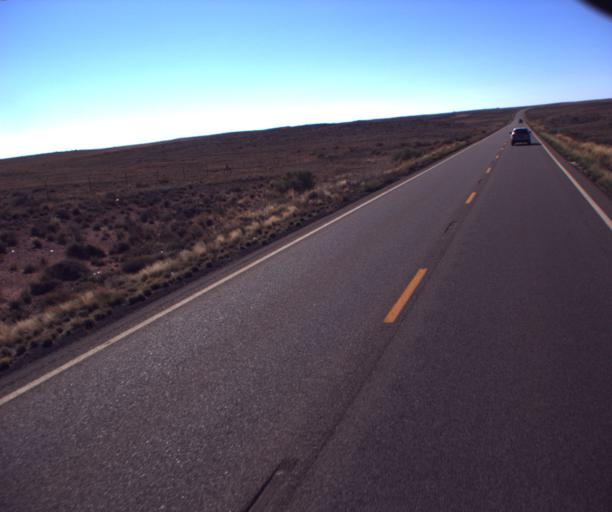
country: US
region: Arizona
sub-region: Navajo County
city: Dilkon
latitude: 35.2486
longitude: -110.4301
